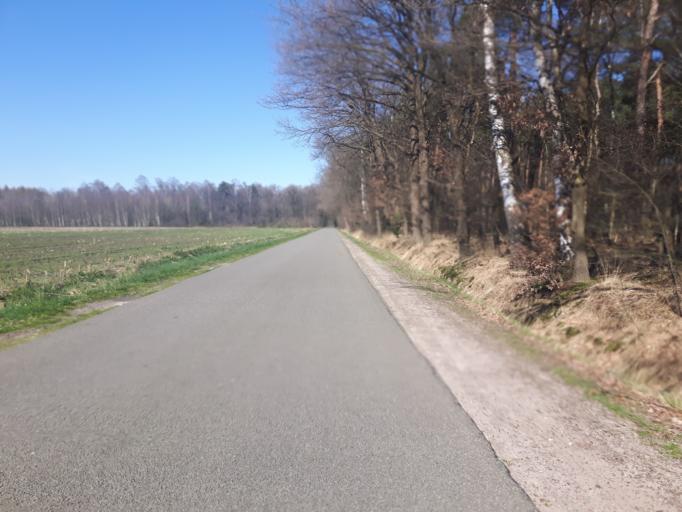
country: NL
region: Overijssel
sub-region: Gemeente Enschede
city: Enschede
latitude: 52.1654
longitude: 6.8272
